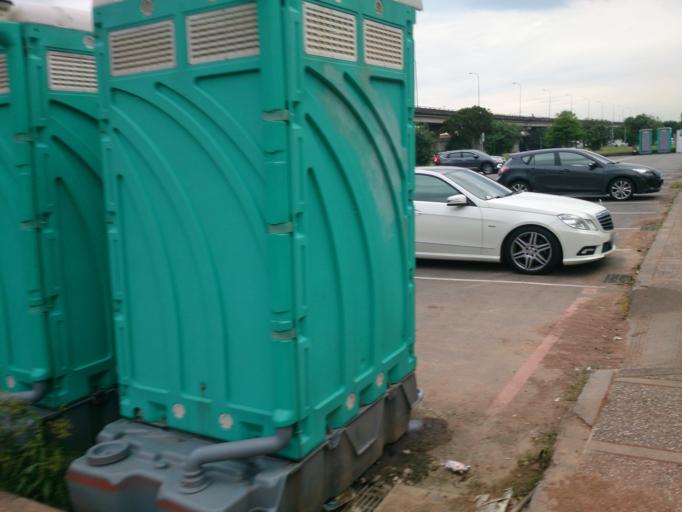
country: TW
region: Taipei
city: Taipei
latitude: 25.0739
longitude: 121.5508
